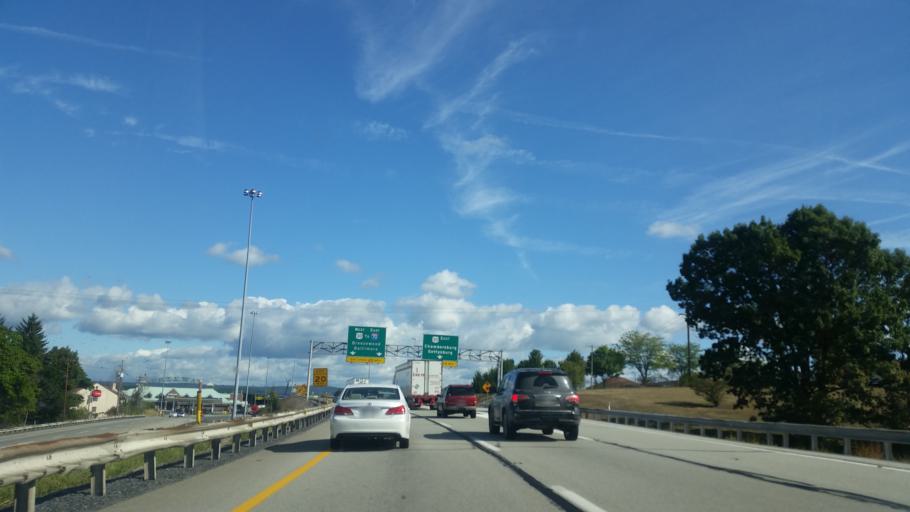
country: US
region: Pennsylvania
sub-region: Bedford County
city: Earlston
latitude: 39.9962
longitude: -78.2334
